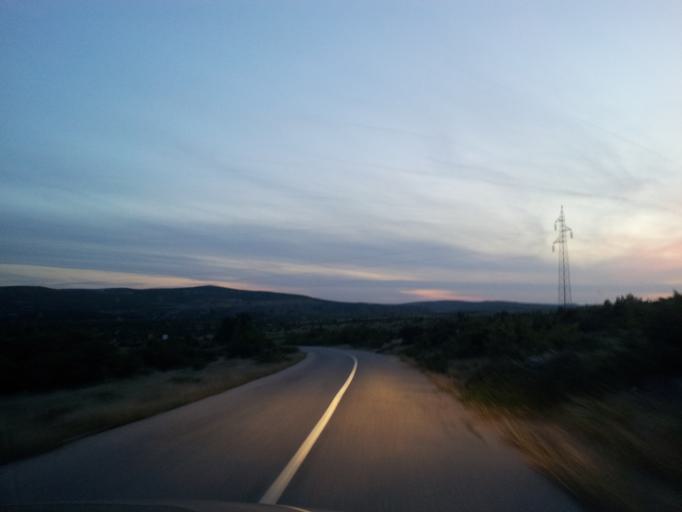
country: HR
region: Zadarska
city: Obrovac
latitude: 44.2204
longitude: 15.6698
